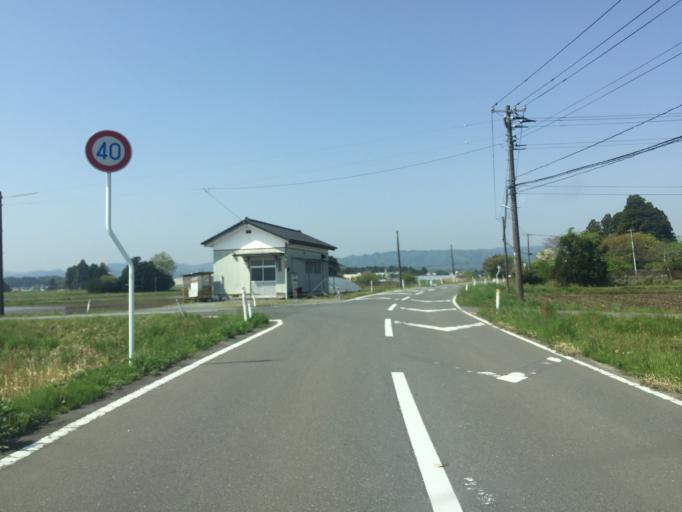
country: JP
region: Miyagi
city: Marumori
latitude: 37.7705
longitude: 140.9543
